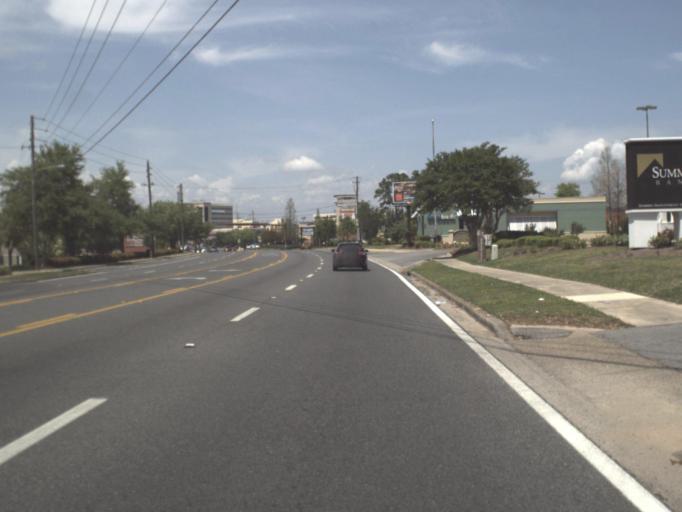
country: US
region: Florida
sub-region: Escambia County
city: Brent
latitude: 30.4692
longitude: -87.2064
